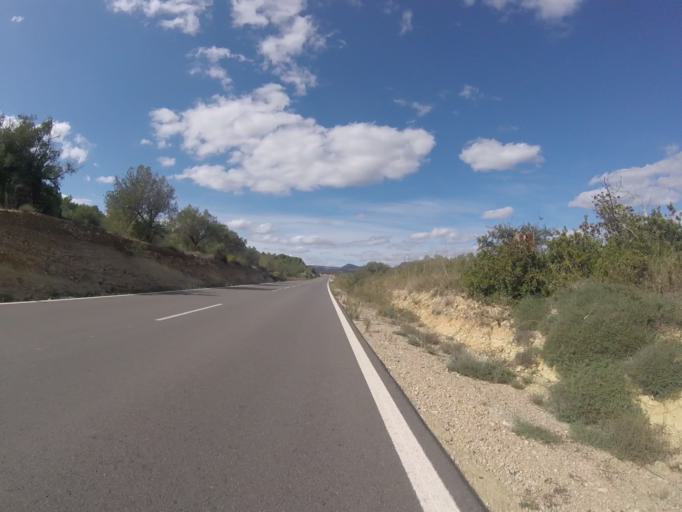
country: ES
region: Valencia
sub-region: Provincia de Castello
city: Chert/Xert
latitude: 40.4374
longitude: 0.1271
